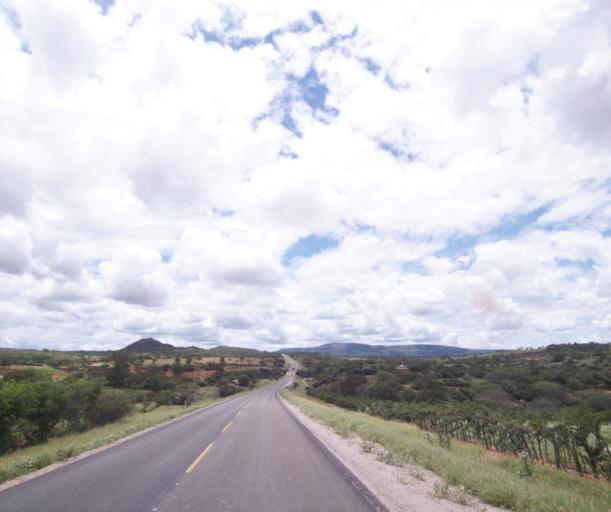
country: BR
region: Bahia
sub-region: Brumado
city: Brumado
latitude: -14.1506
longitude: -41.4920
